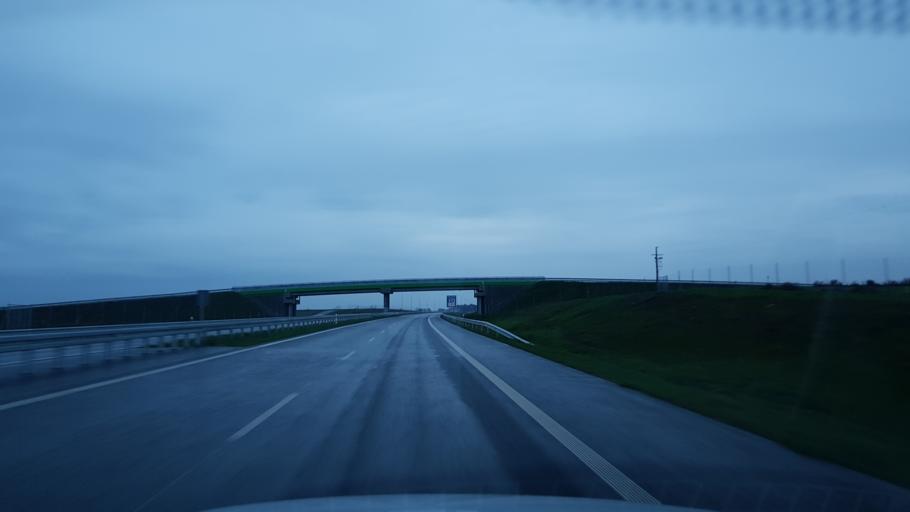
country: PL
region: West Pomeranian Voivodeship
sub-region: Powiat gryficki
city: Brojce
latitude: 53.9774
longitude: 15.4281
